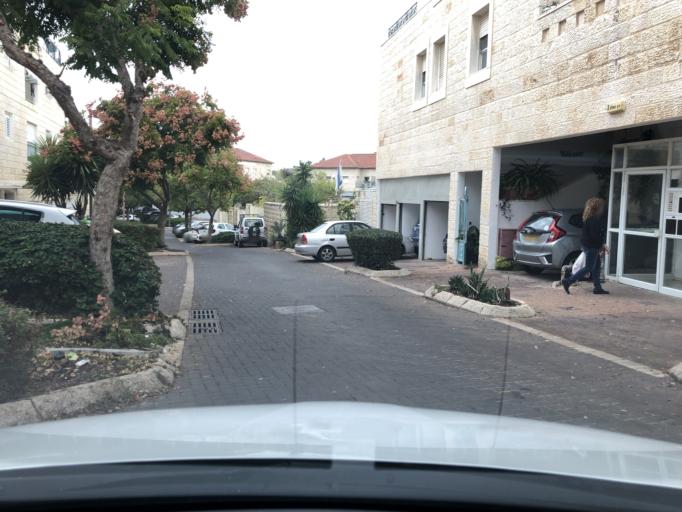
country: IL
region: Central District
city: Modiin
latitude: 31.9046
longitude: 35.0125
